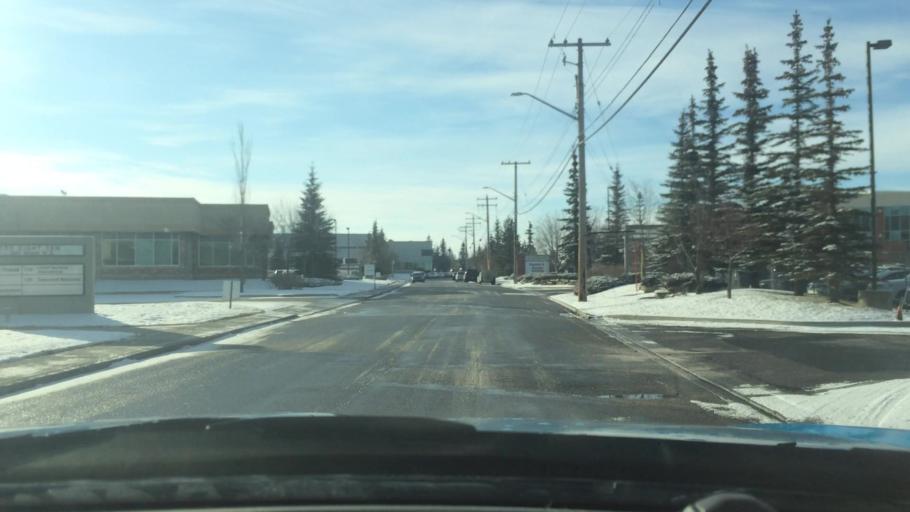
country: CA
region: Alberta
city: Calgary
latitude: 51.1206
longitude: -114.0432
